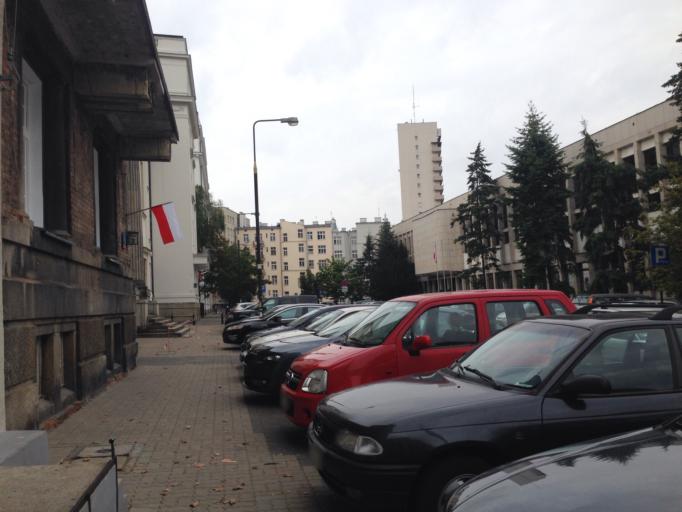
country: PL
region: Masovian Voivodeship
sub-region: Warszawa
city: Srodmiescie
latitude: 52.2351
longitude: 21.0221
